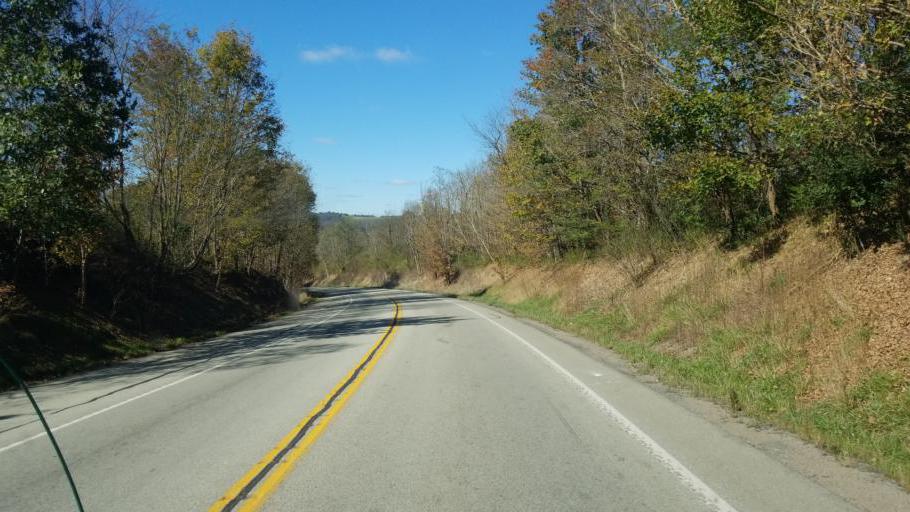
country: US
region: Pennsylvania
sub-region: Somerset County
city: Friedens
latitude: 40.0959
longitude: -78.9293
